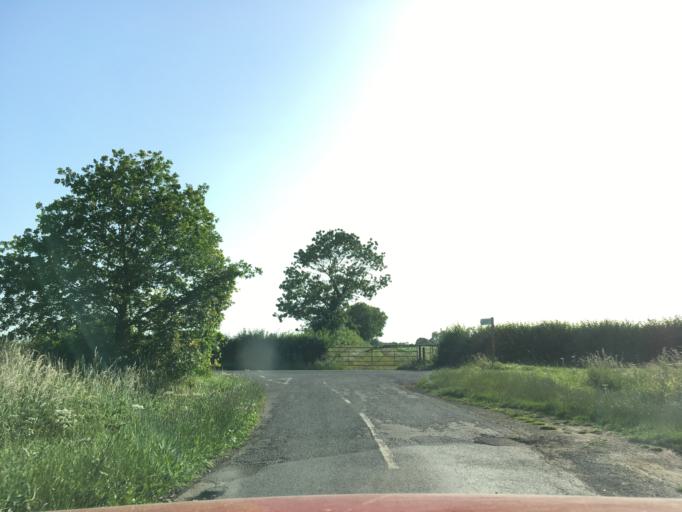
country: GB
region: England
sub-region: Gloucestershire
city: Fairford
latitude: 51.7195
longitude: -1.7668
